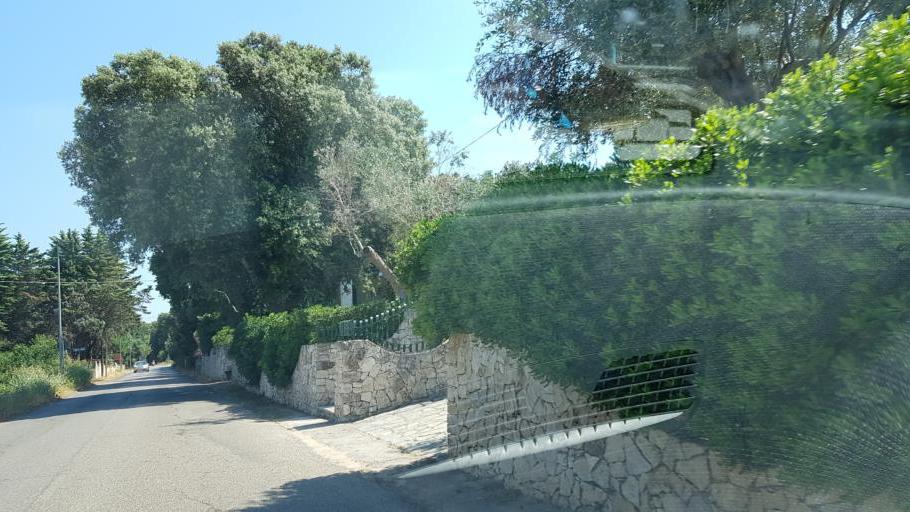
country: IT
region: Apulia
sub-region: Provincia di Lecce
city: Nardo
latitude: 40.1489
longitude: 17.9827
